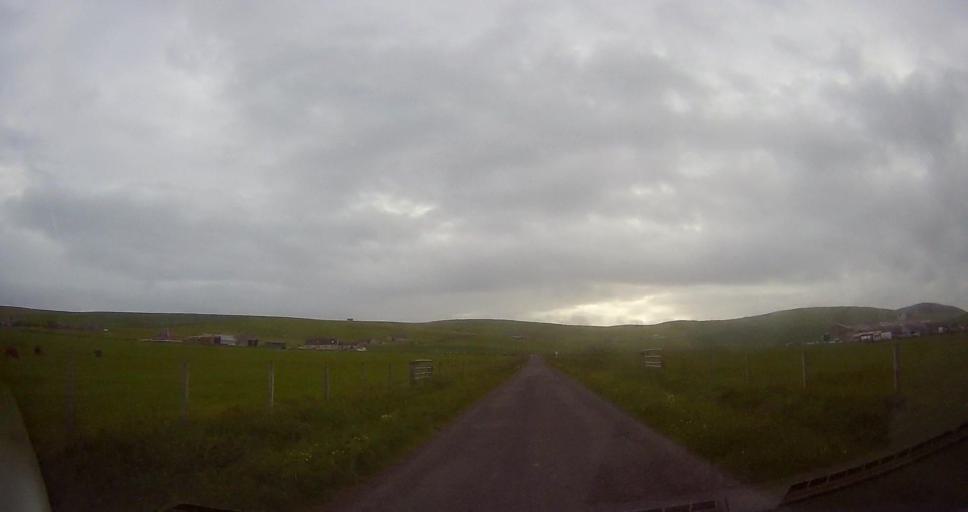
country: GB
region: Scotland
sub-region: Orkney Islands
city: Stromness
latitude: 58.9901
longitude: -3.2854
